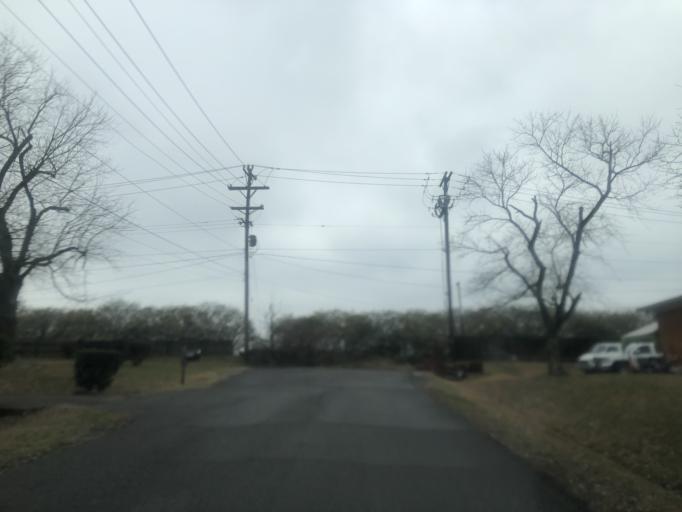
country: US
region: Tennessee
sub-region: Davidson County
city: Lakewood
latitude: 36.1515
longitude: -86.6630
